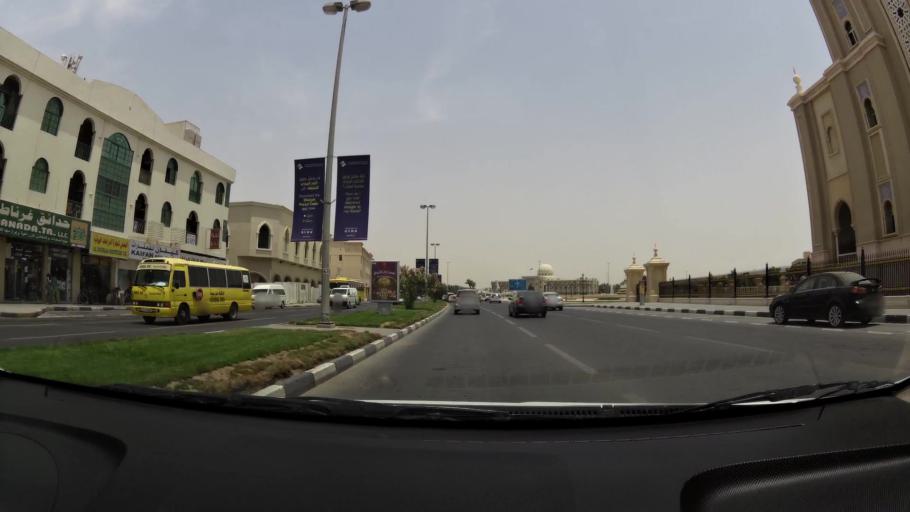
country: AE
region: Ash Shariqah
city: Sharjah
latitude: 25.3580
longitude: 55.4016
